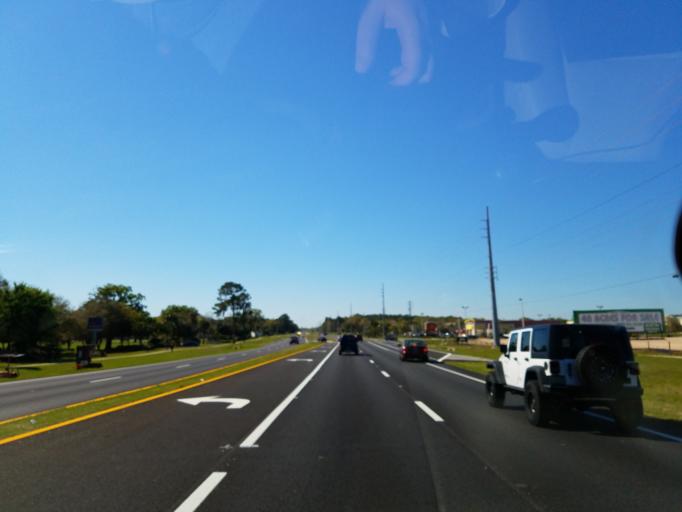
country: US
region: Florida
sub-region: Marion County
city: Ocala
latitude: 29.2126
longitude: -82.1975
